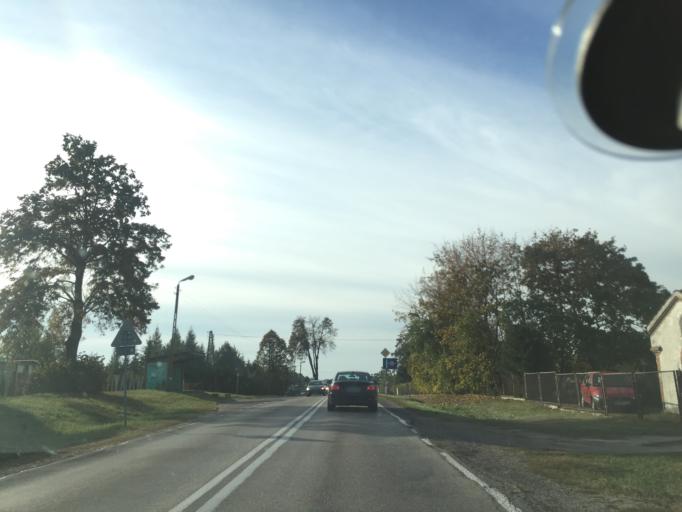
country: PL
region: Warmian-Masurian Voivodeship
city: Dobre Miasto
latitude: 54.0276
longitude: 20.4101
